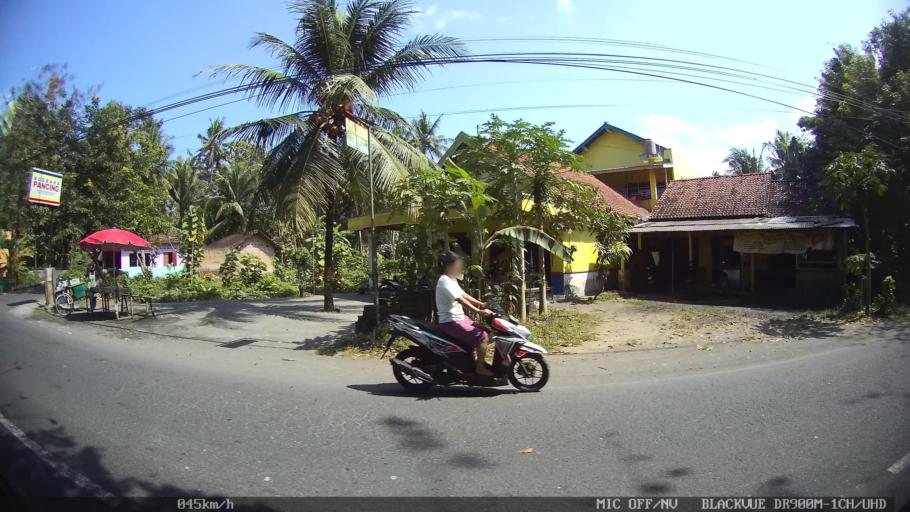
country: ID
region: Daerah Istimewa Yogyakarta
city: Srandakan
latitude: -7.9434
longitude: 110.2294
